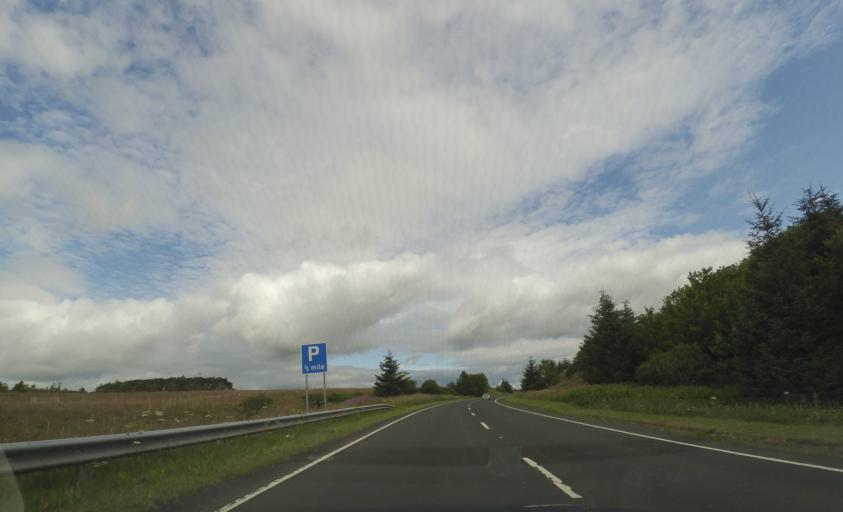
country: GB
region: Scotland
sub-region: The Scottish Borders
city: Selkirk
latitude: 55.5074
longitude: -2.8443
